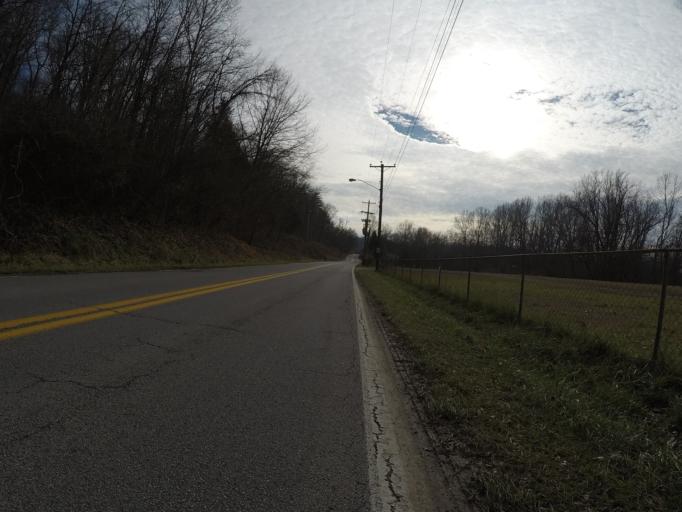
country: US
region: West Virginia
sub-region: Cabell County
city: Barboursville
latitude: 38.4141
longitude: -82.2950
